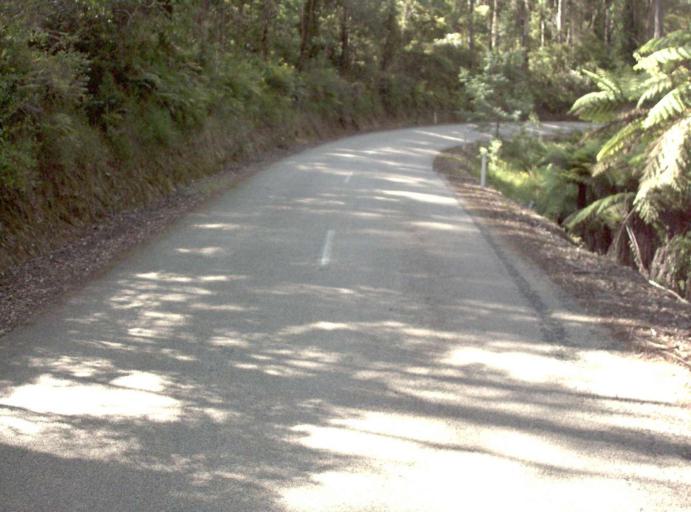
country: AU
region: Victoria
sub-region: East Gippsland
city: Lakes Entrance
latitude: -37.4307
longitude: 148.5983
